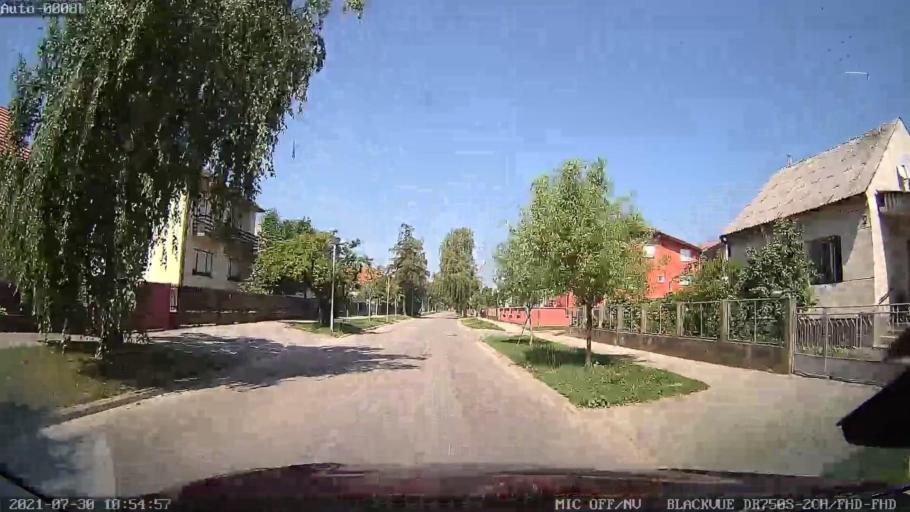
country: HR
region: Varazdinska
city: Varazdin
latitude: 46.3148
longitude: 16.3205
